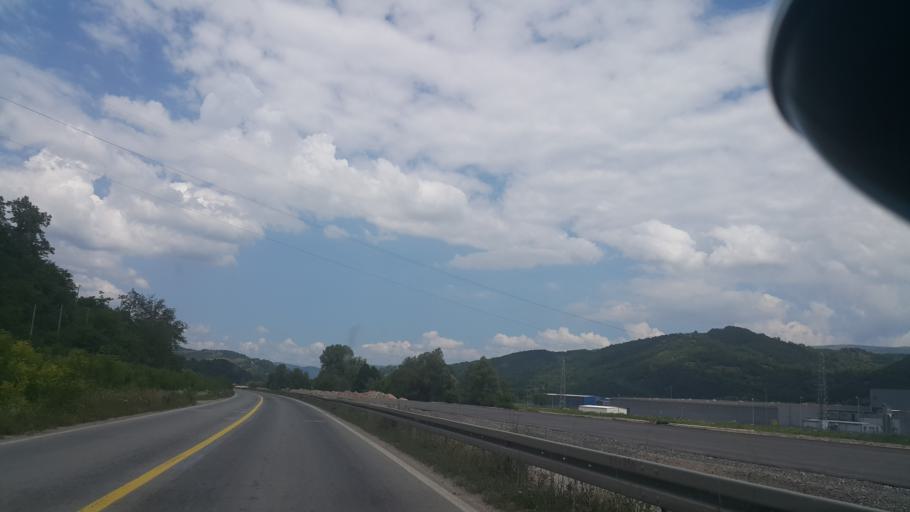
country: RS
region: Central Serbia
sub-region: Pirotski Okrug
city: Pirot
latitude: 43.1729
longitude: 22.5726
